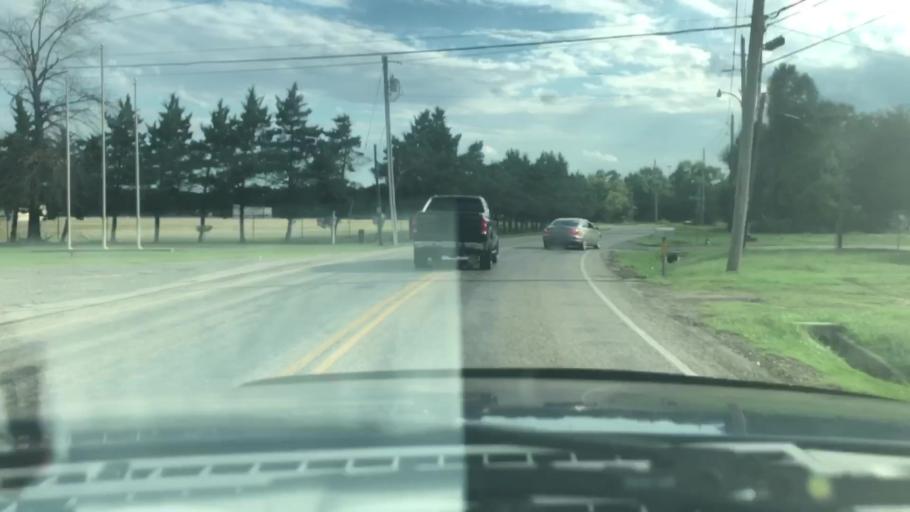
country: US
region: Texas
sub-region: Bowie County
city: Texarkana
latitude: 33.3934
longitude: -94.0649
